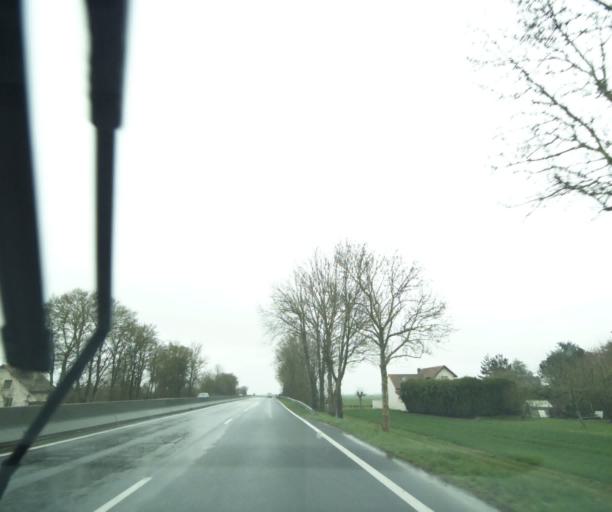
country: FR
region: Ile-de-France
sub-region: Departement de l'Essonne
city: Angerville
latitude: 48.3097
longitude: 1.9926
